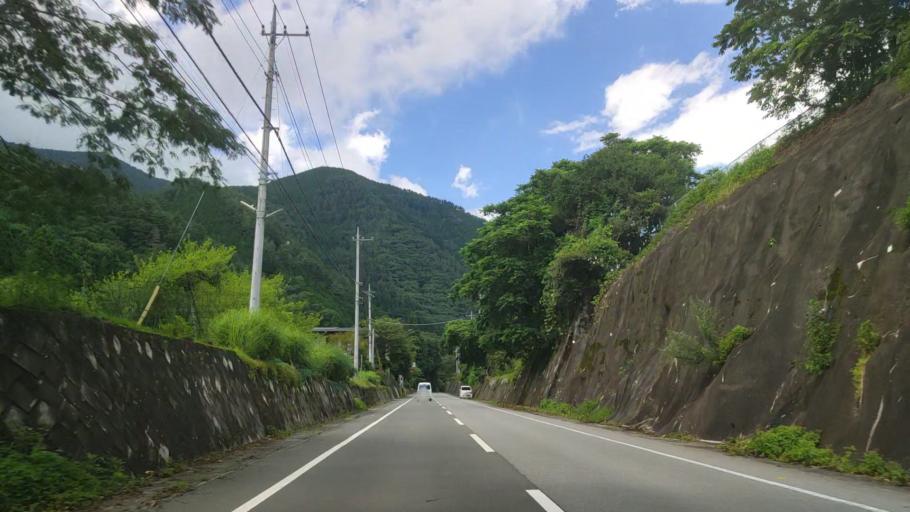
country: JP
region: Yamanashi
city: Enzan
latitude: 35.7920
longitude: 138.7390
